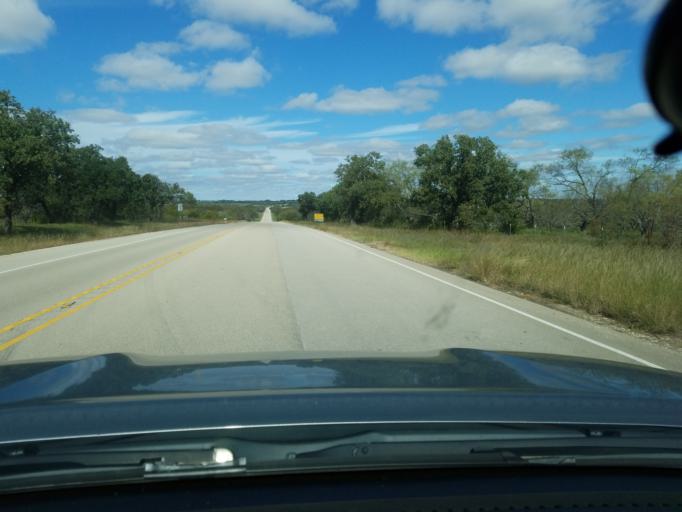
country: US
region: Texas
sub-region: Hamilton County
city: Hamilton
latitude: 31.5972
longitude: -98.1574
